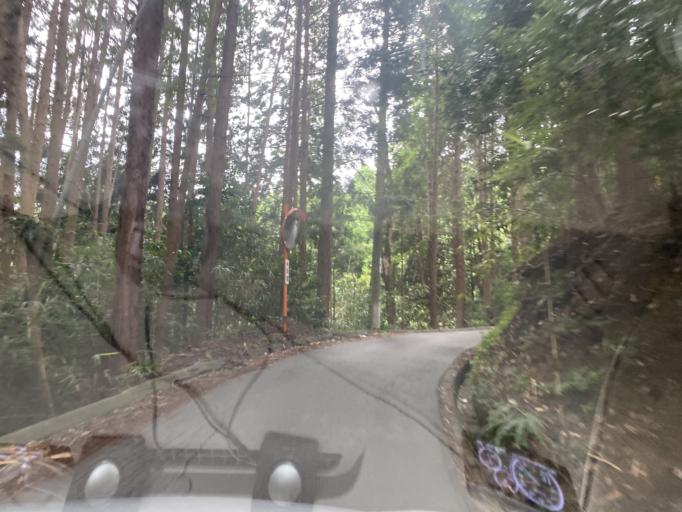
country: JP
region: Nara
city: Nara-shi
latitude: 34.6859
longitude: 135.8963
